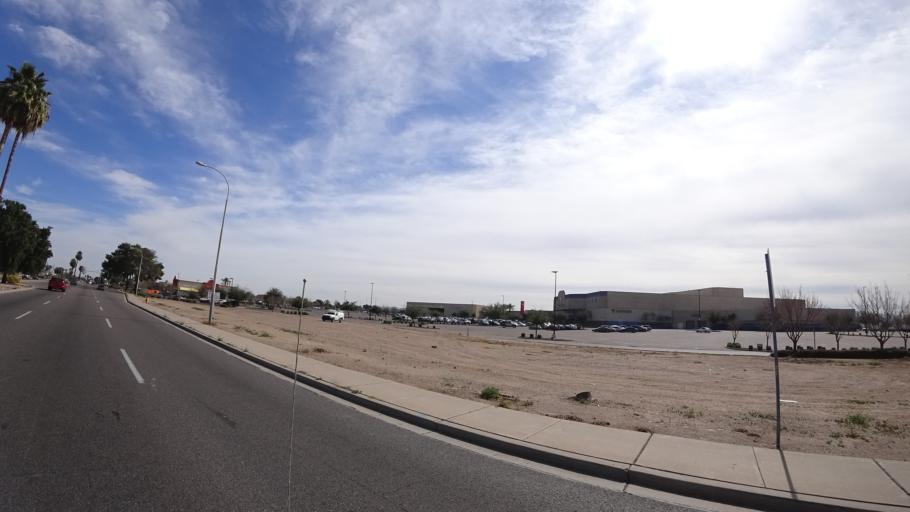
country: US
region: Arizona
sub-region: Maricopa County
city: Tolleson
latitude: 33.4800
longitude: -112.2269
